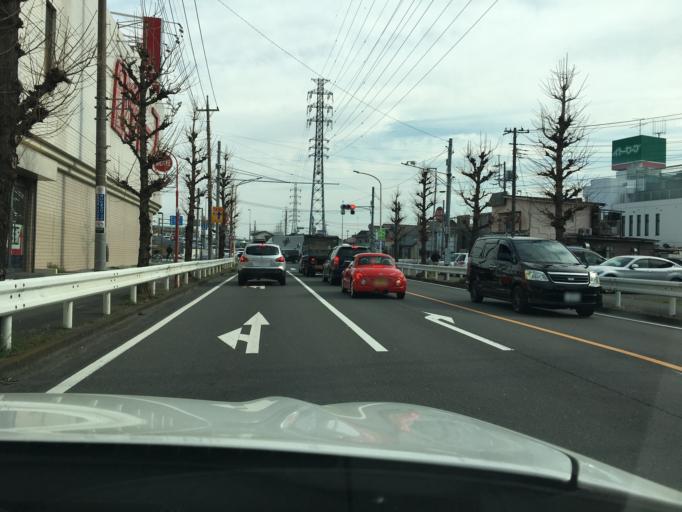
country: JP
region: Saitama
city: Kawagoe
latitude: 35.9064
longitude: 139.4729
